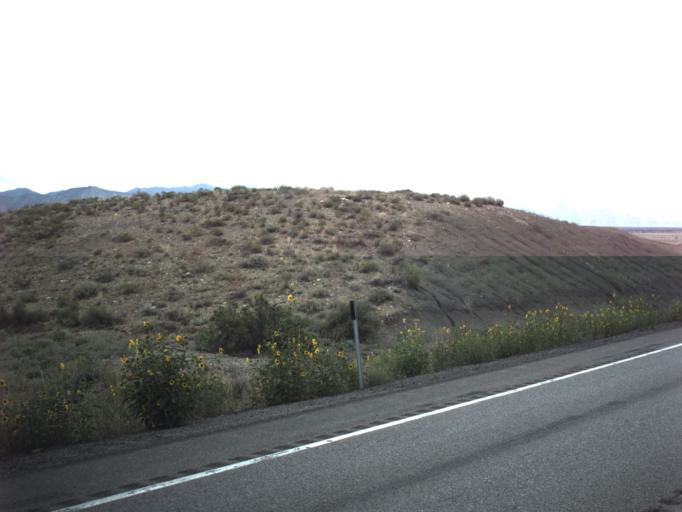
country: US
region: Utah
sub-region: Carbon County
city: East Carbon City
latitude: 39.4630
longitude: -110.4897
